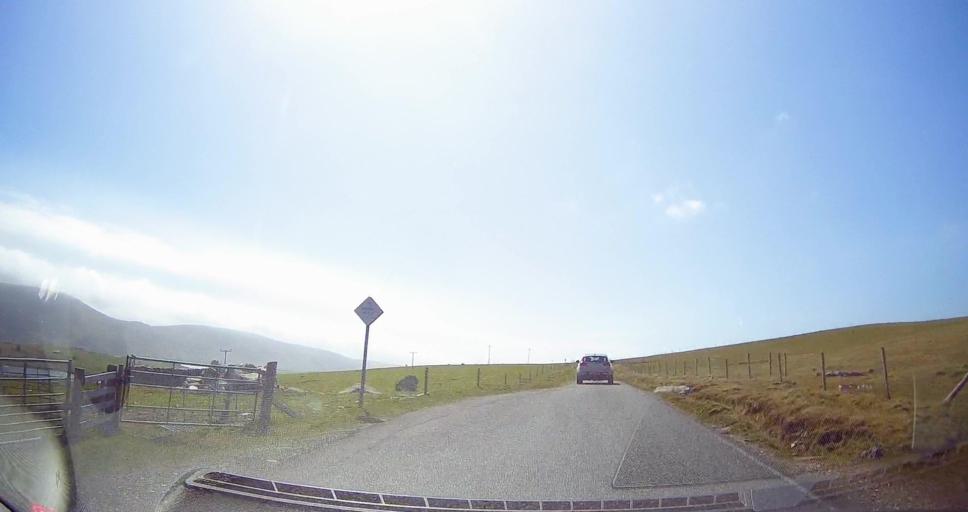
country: GB
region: Scotland
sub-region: Shetland Islands
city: Sandwick
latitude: 60.0777
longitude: -1.3382
